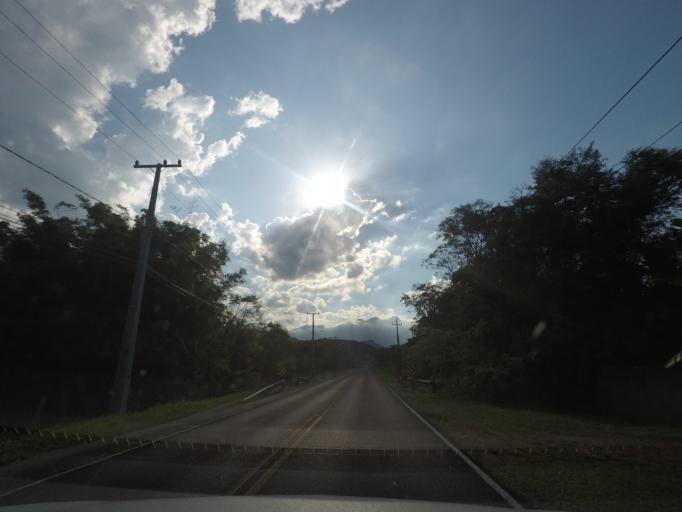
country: BR
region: Parana
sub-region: Antonina
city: Antonina
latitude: -25.4492
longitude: -48.8686
